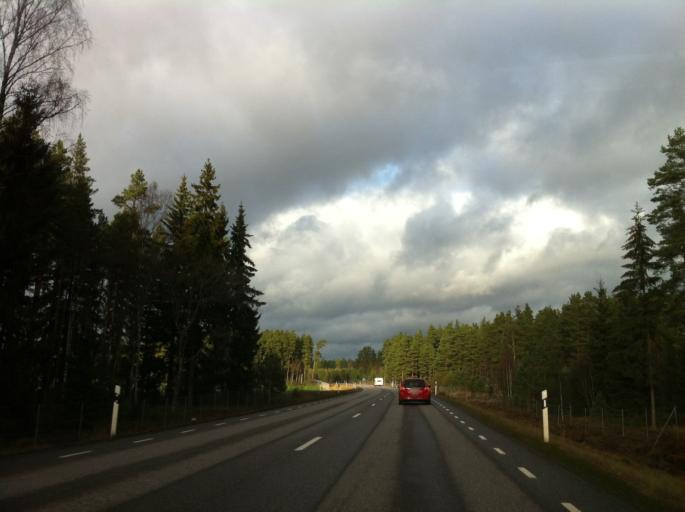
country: SE
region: Kalmar
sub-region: Vimmerby Kommun
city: Vimmerby
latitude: 57.6091
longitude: 15.8438
